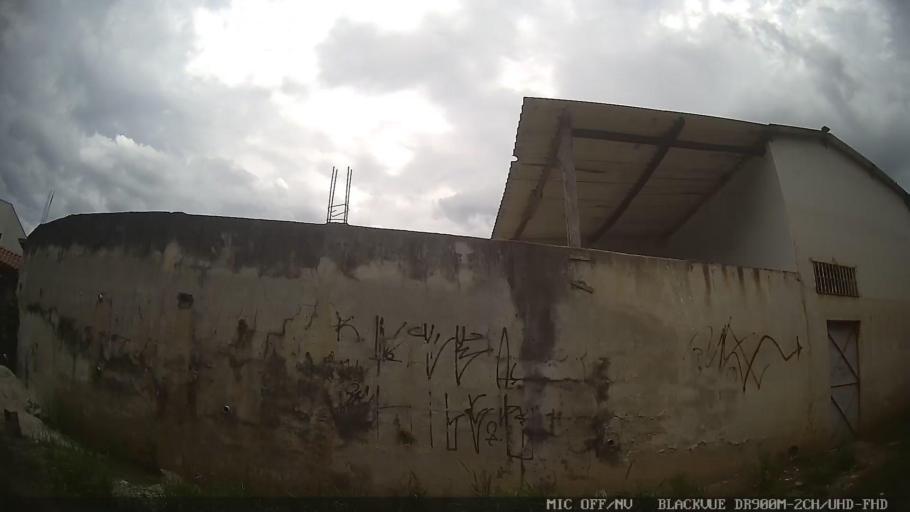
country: BR
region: Sao Paulo
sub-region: Suzano
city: Suzano
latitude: -23.6342
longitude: -46.2775
